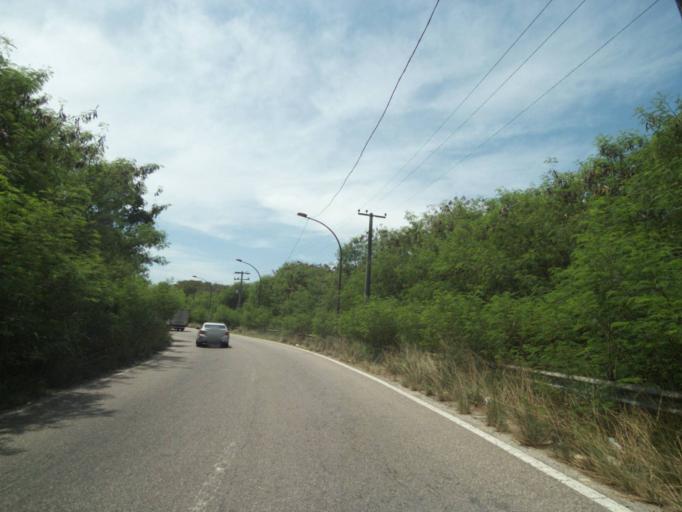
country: BR
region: Rio de Janeiro
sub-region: Duque De Caxias
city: Duque de Caxias
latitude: -22.8095
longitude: -43.2904
